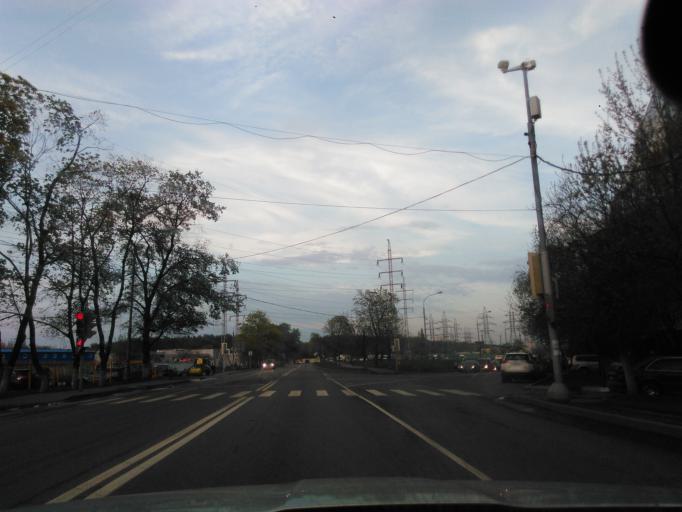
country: RU
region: Moscow
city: Lyublino
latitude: 55.6819
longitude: 37.7751
